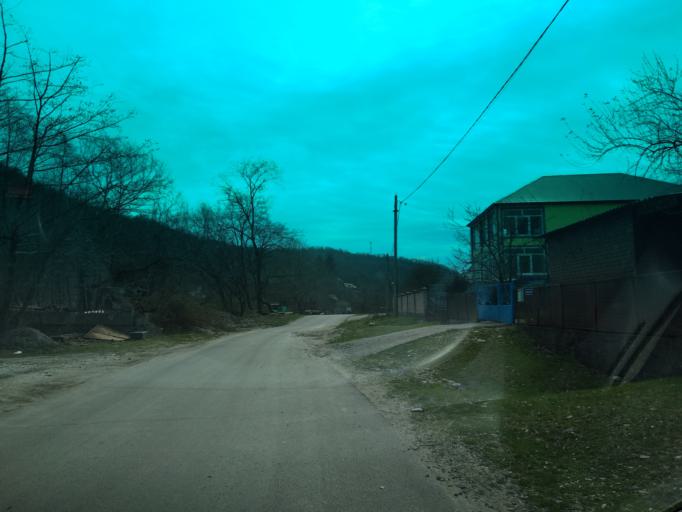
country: RU
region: Krasnodarskiy
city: Shepsi
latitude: 44.0631
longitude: 39.1374
